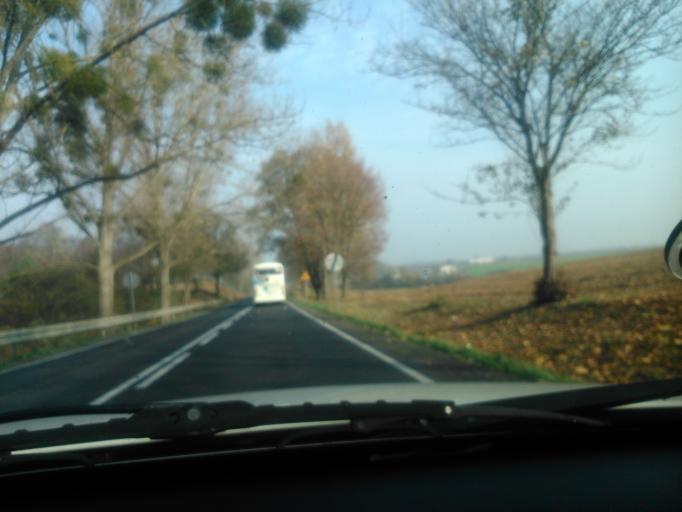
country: PL
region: Kujawsko-Pomorskie
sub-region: Powiat brodnicki
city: Bobrowo
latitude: 53.2472
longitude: 19.3025
